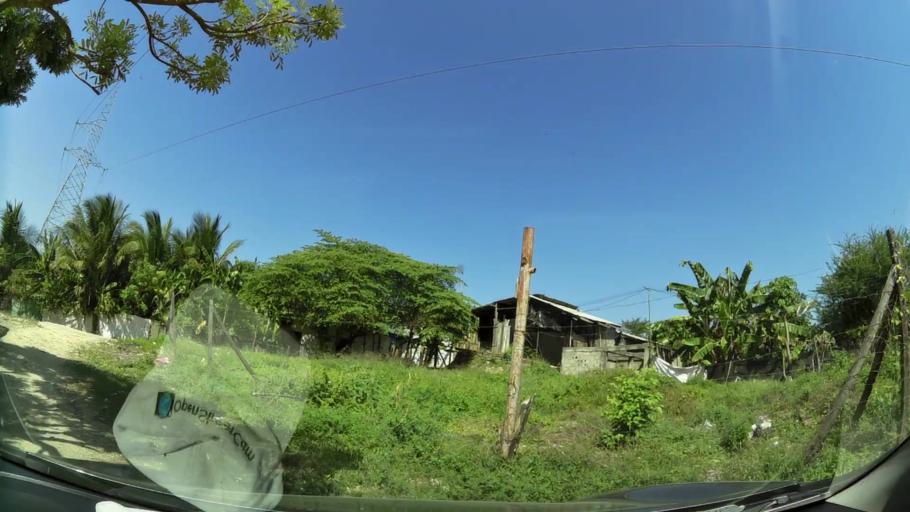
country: CO
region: Bolivar
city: Cartagena
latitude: 10.3596
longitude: -75.4887
